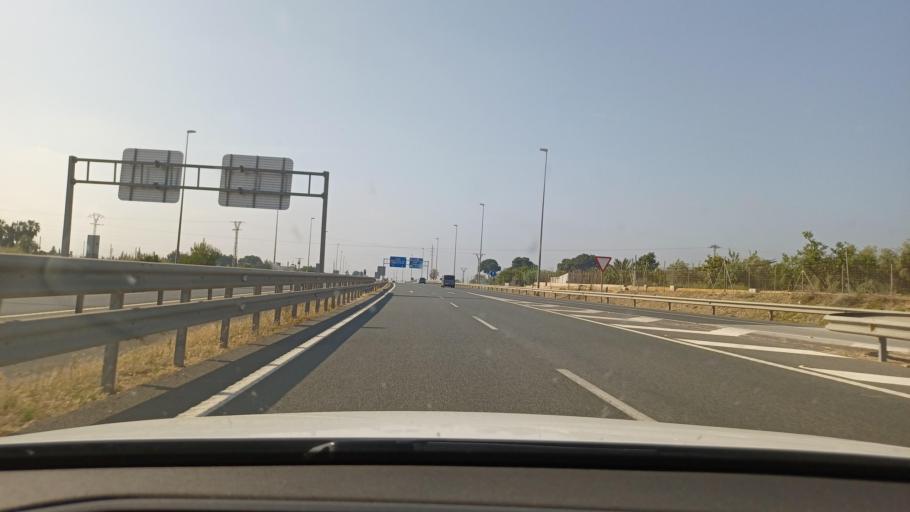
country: ES
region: Valencia
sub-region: Provincia de Alicante
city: Elche
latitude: 38.2842
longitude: -0.6645
